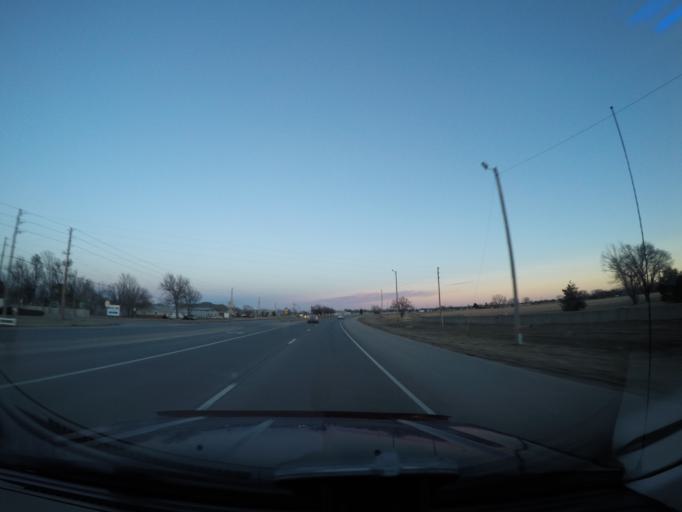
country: US
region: Kansas
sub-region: Sedgwick County
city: Maize
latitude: 37.7233
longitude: -97.4132
